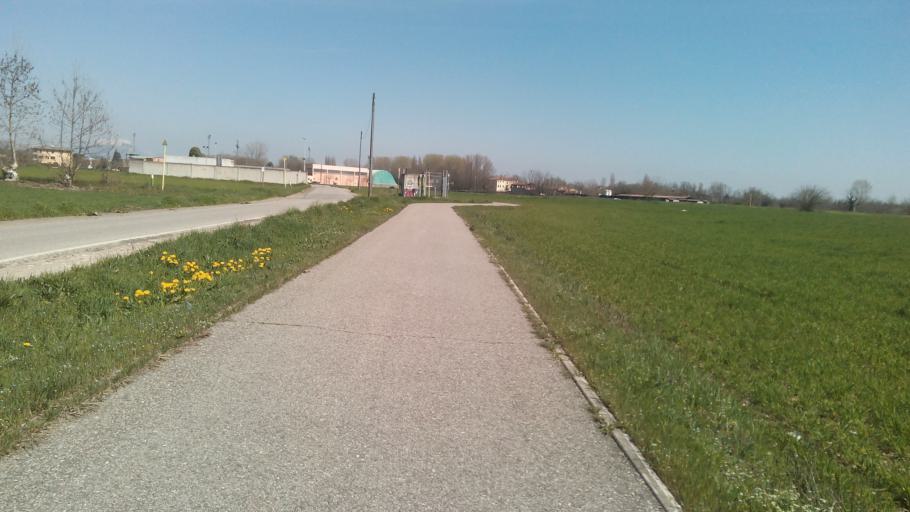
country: IT
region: Lombardy
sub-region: Provincia di Mantova
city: Goito
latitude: 45.2437
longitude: 10.6685
